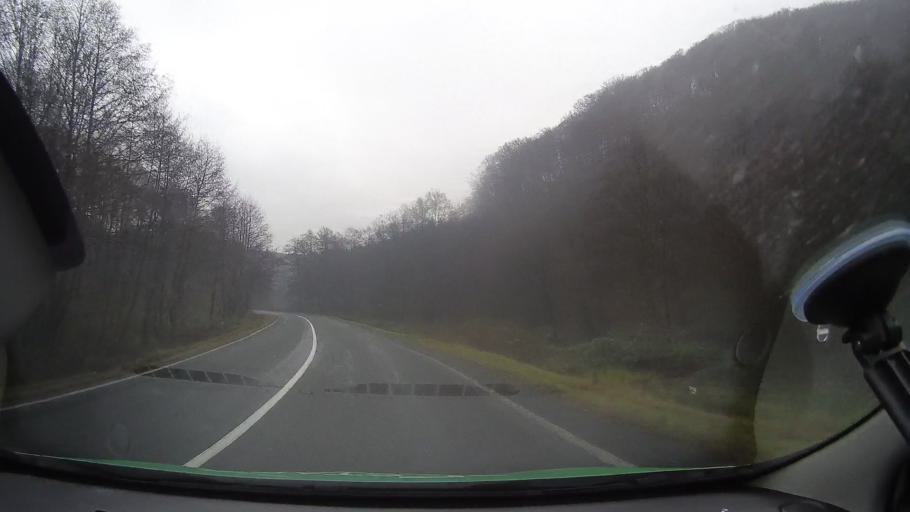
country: RO
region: Arad
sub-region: Comuna Plescuta
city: Plescuta
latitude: 46.3172
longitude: 22.4630
